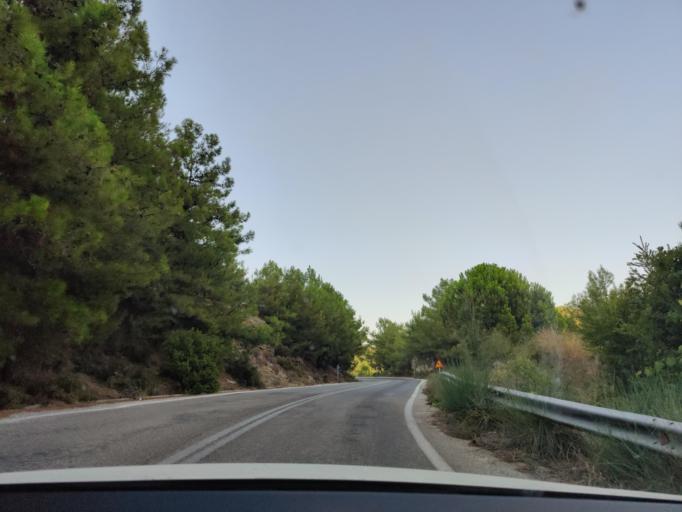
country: GR
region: East Macedonia and Thrace
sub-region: Nomos Kavalas
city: Potamia
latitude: 40.6192
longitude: 24.7586
